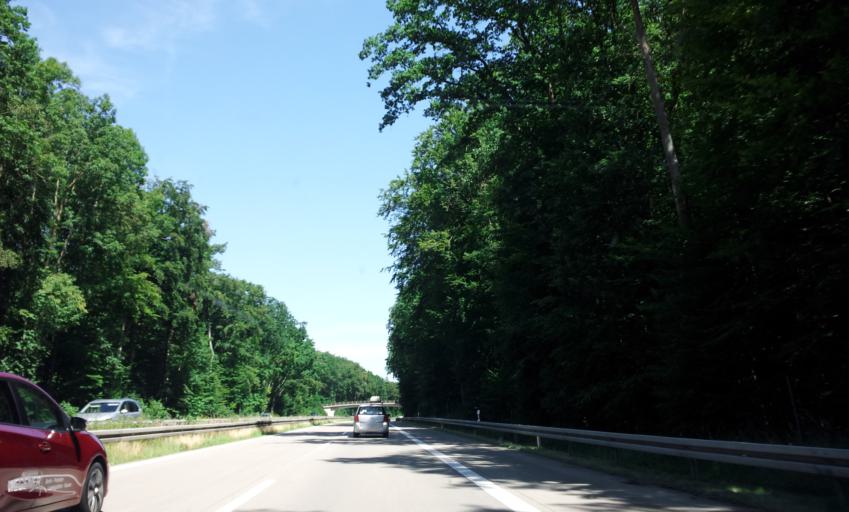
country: DE
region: Brandenburg
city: Gramzow
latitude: 53.1484
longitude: 13.8989
